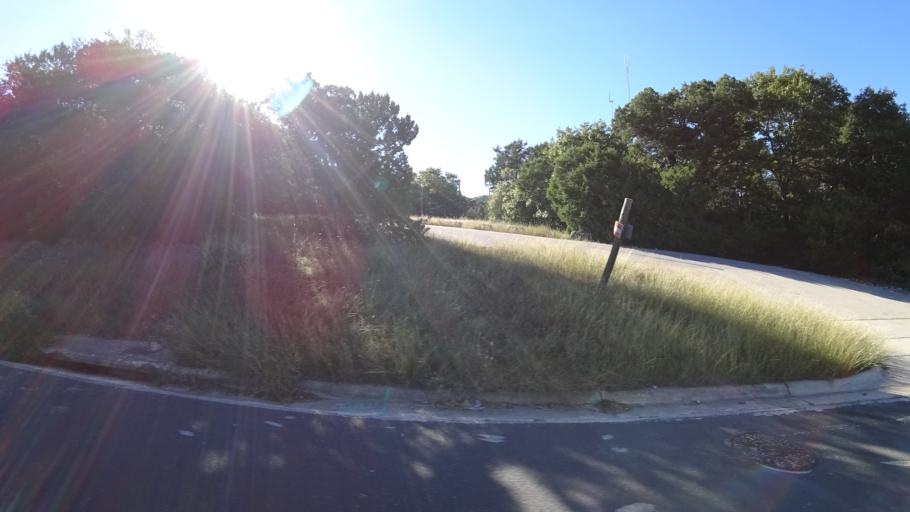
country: US
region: Texas
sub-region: Travis County
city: West Lake Hills
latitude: 30.3327
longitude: -97.7997
